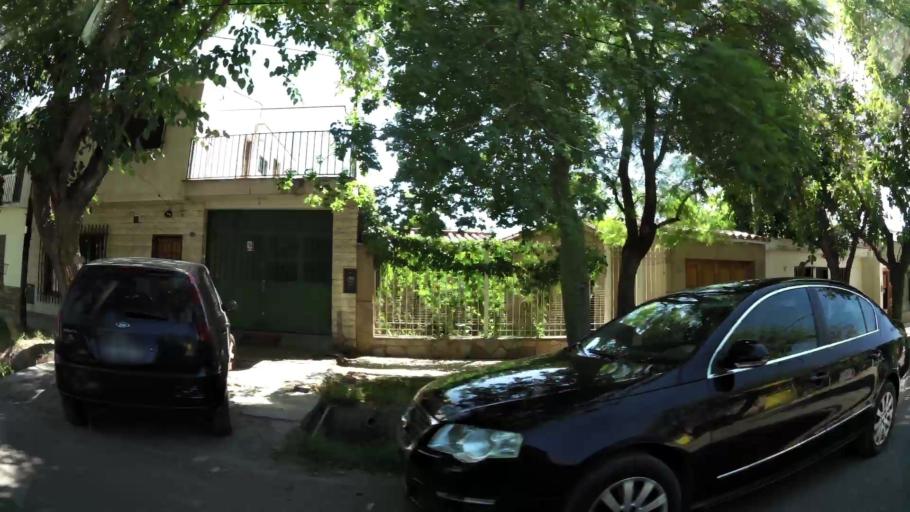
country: AR
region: Mendoza
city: Mendoza
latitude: -32.8925
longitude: -68.8053
